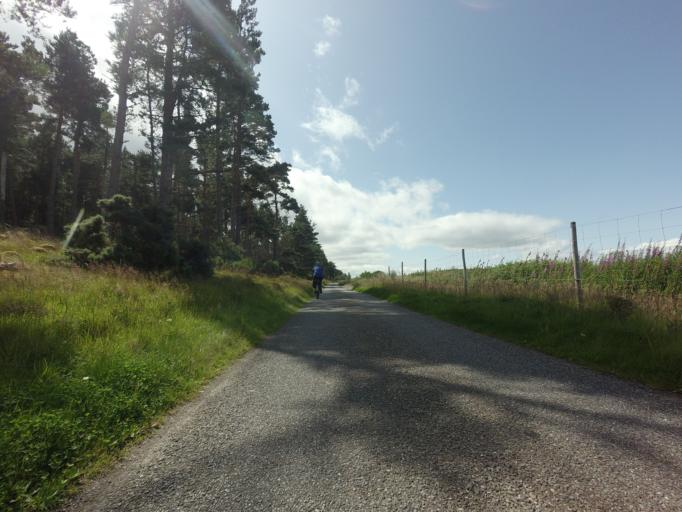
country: GB
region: Scotland
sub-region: Highland
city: Fortrose
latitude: 57.4848
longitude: -4.0318
